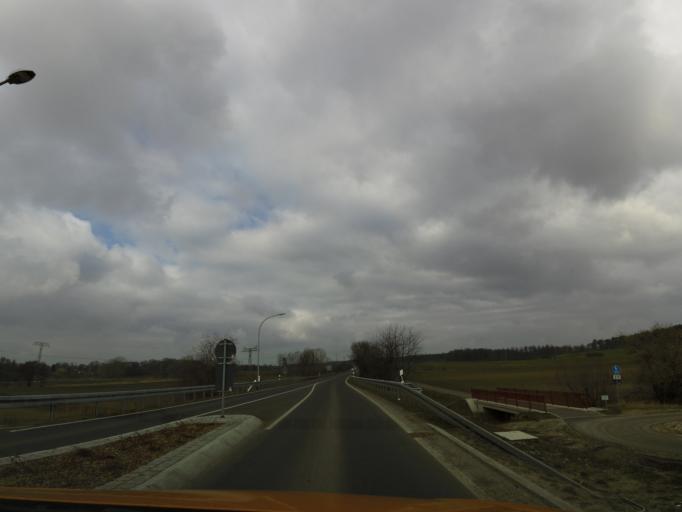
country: DE
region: Brandenburg
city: Werder
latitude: 52.4536
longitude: 12.9790
